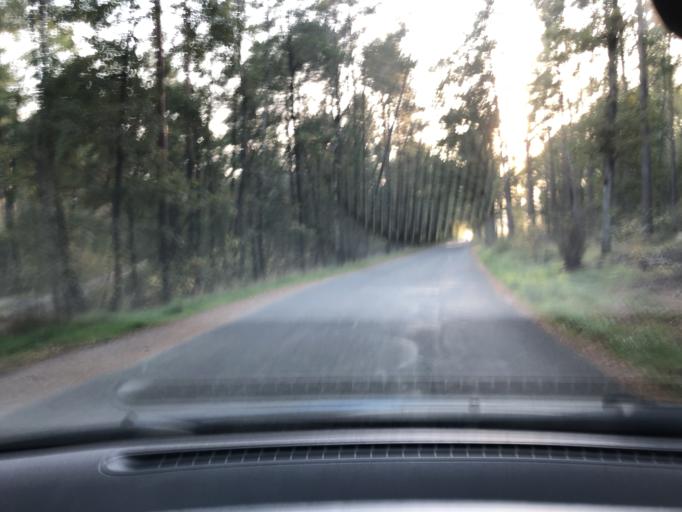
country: DE
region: Lower Saxony
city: Hitzacker
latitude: 53.1297
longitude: 11.0250
